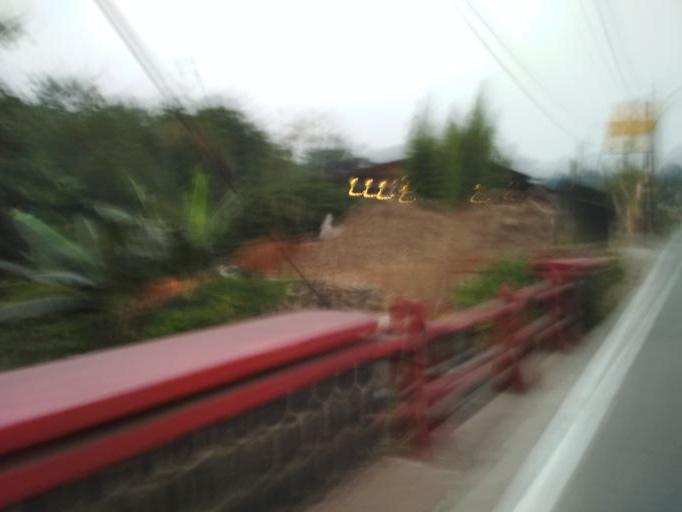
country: ID
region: West Java
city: Caringin
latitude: -6.6632
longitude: 106.8452
